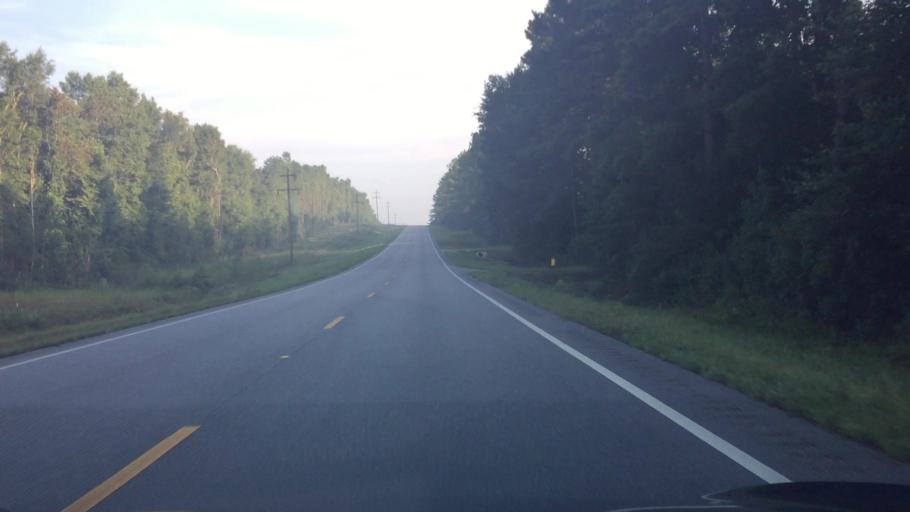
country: US
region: Alabama
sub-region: Covington County
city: Florala
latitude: 31.0604
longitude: -86.3944
